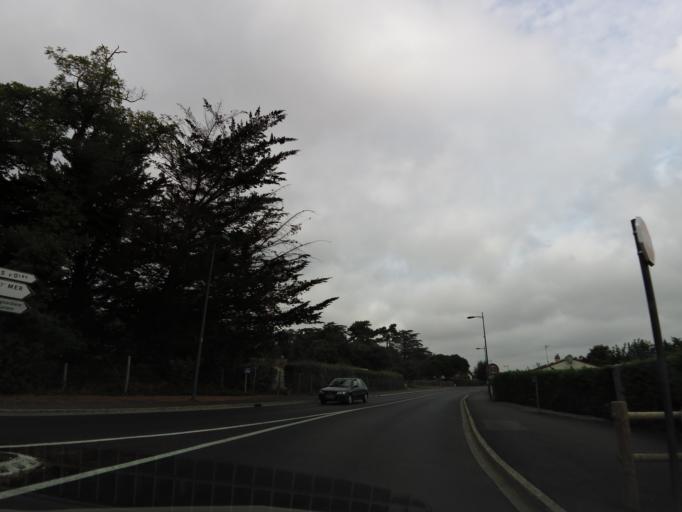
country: FR
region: Pays de la Loire
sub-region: Departement de la Vendee
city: Longeville-sur-Mer
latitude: 46.4088
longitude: -1.4931
